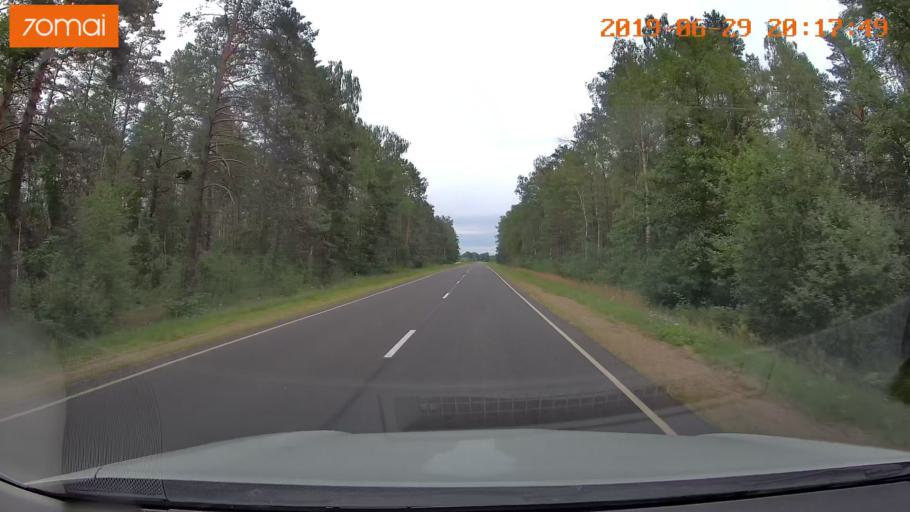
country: BY
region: Brest
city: Asnyezhytsy
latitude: 52.3907
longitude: 26.2239
